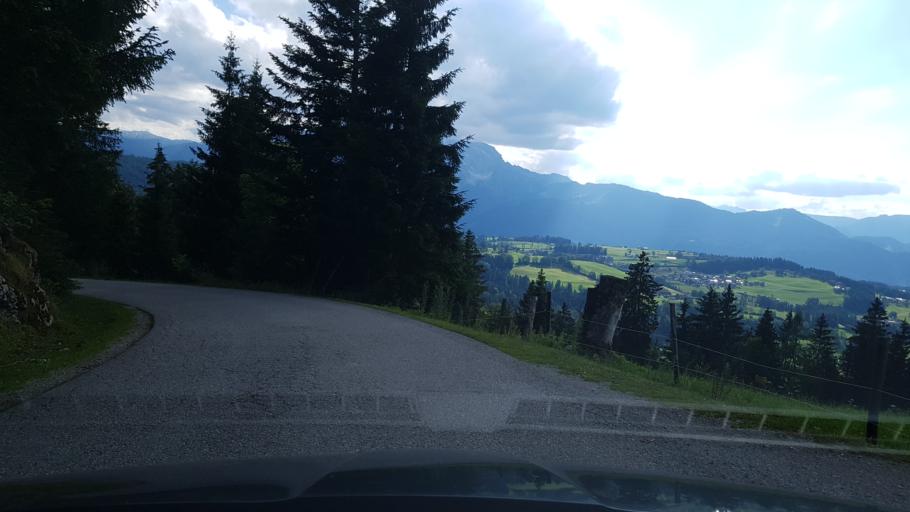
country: AT
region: Salzburg
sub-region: Politischer Bezirk Hallein
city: Scheffau am Tennengebirge
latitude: 47.6452
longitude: 13.2394
